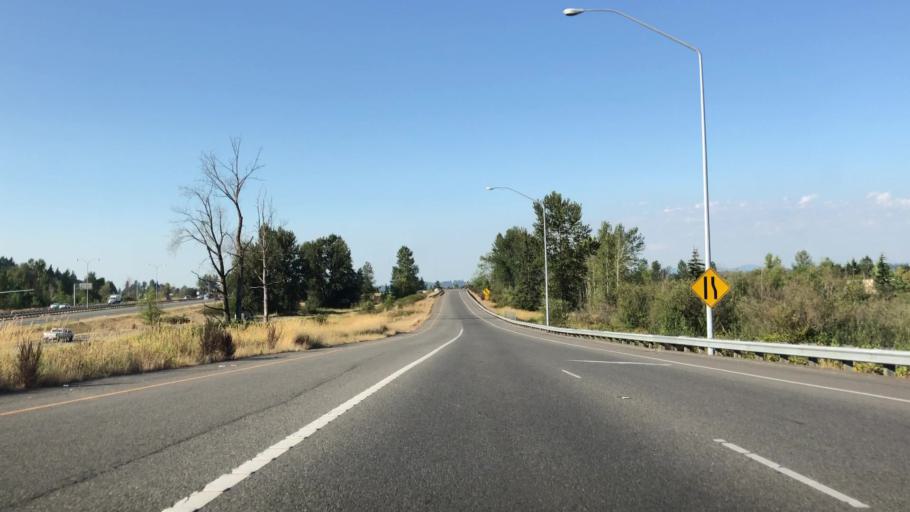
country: US
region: Washington
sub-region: King County
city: Algona
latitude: 47.2967
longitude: -122.2552
